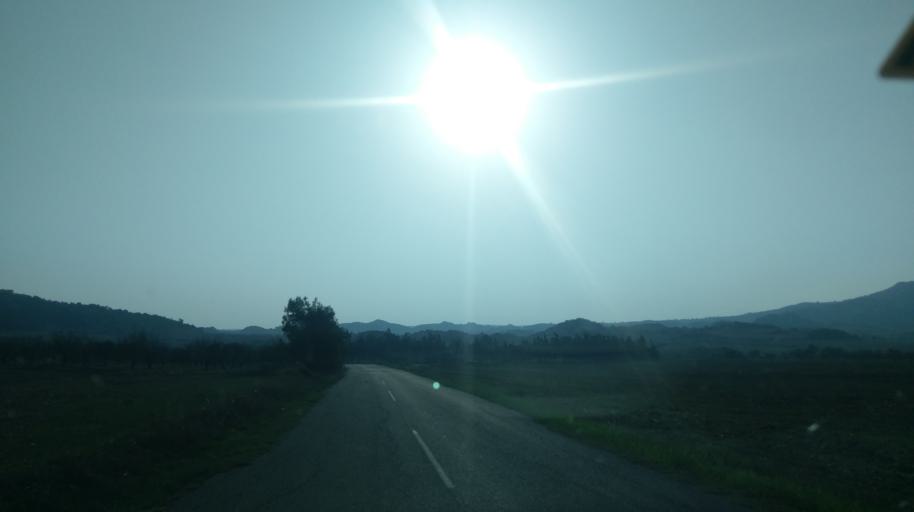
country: CY
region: Ammochostos
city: Leonarisso
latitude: 35.4692
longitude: 34.1030
